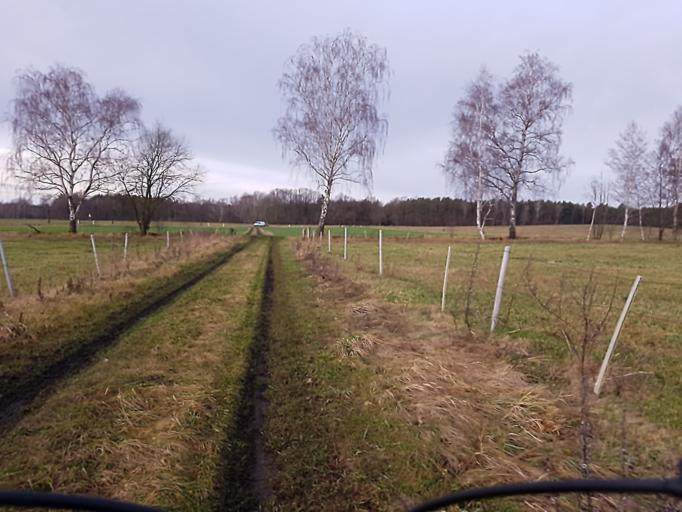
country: DE
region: Brandenburg
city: Schilda
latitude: 51.5798
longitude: 13.4050
